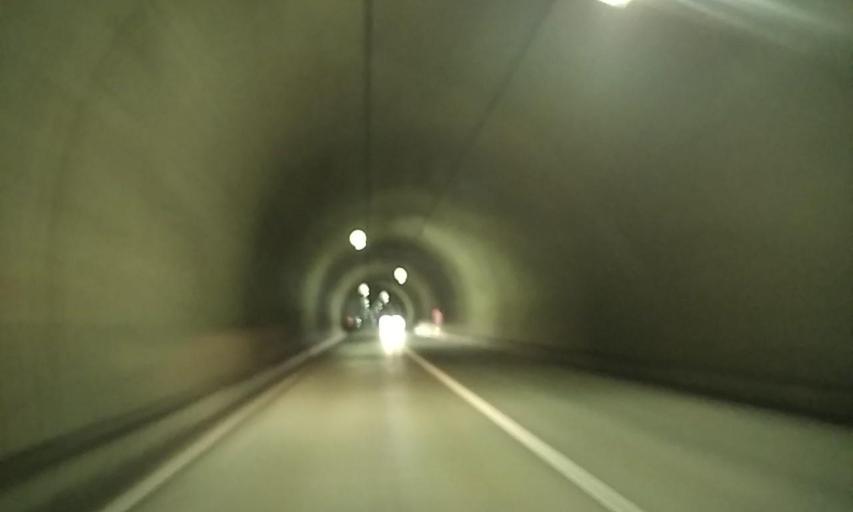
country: JP
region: Wakayama
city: Shingu
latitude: 33.8822
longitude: 135.8780
